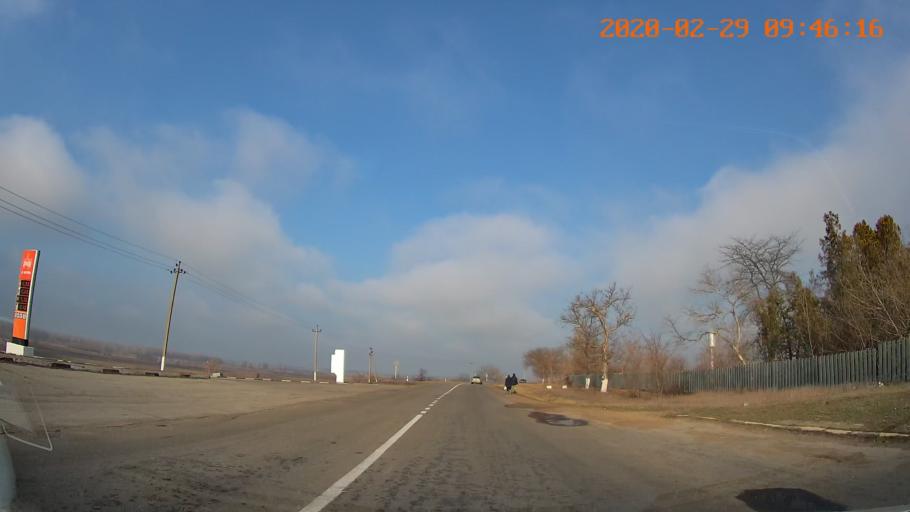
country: MD
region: Telenesti
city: Crasnoe
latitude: 46.6654
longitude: 29.8003
